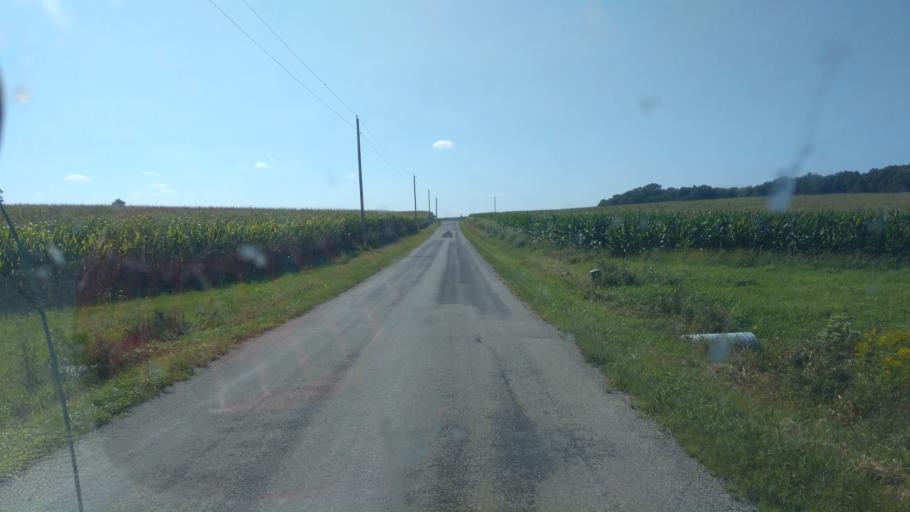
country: US
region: Ohio
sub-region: Ashland County
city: Ashland
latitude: 40.9598
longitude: -82.3365
